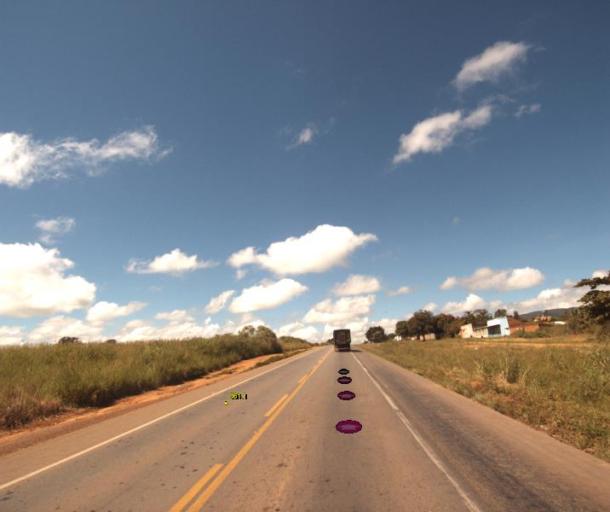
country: BR
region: Goias
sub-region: Jaragua
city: Jaragua
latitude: -15.7493
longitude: -49.3173
